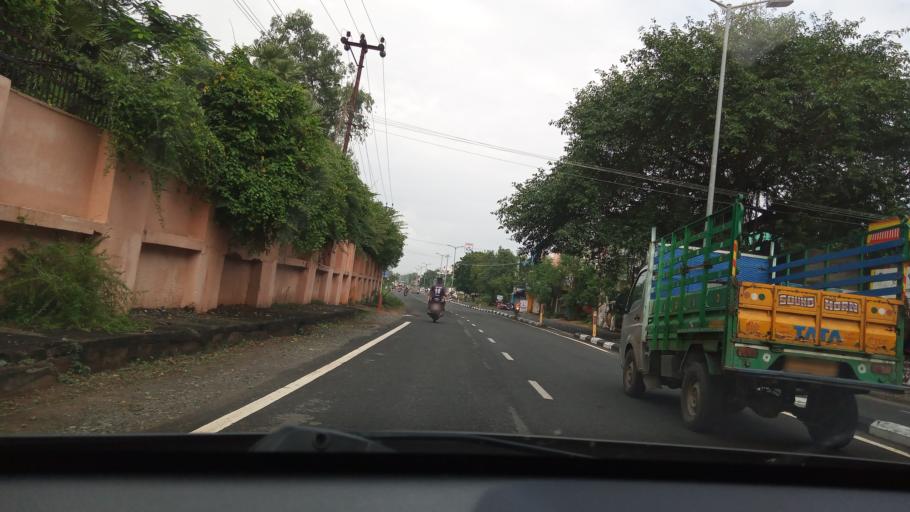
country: IN
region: Tamil Nadu
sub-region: Villupuram
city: Auroville
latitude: 12.0170
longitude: 79.8590
